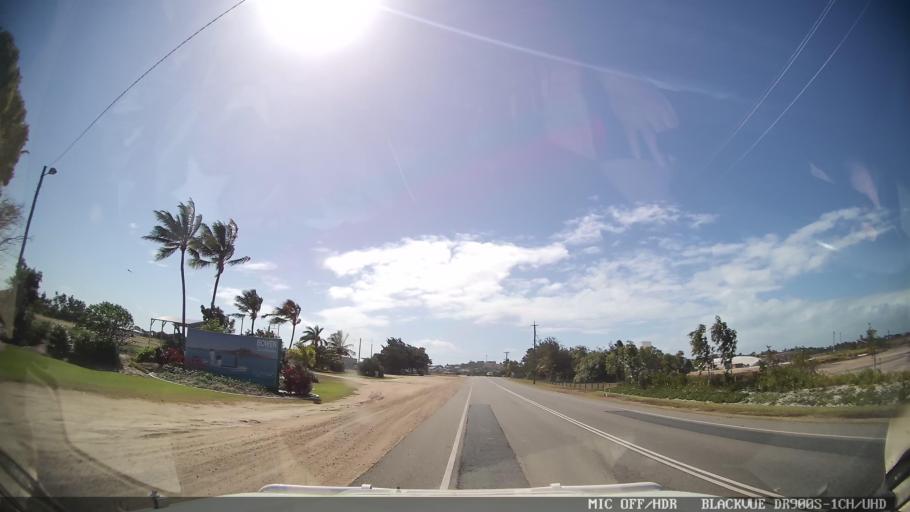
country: AU
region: Queensland
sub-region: Whitsunday
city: Bowen
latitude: -20.0137
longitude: 148.2235
